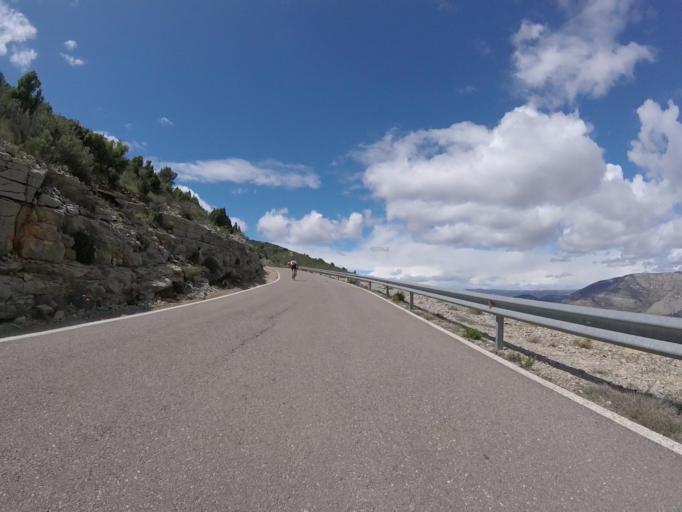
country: ES
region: Valencia
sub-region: Provincia de Castello
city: Sierra-Engarceran
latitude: 40.2780
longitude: -0.0299
